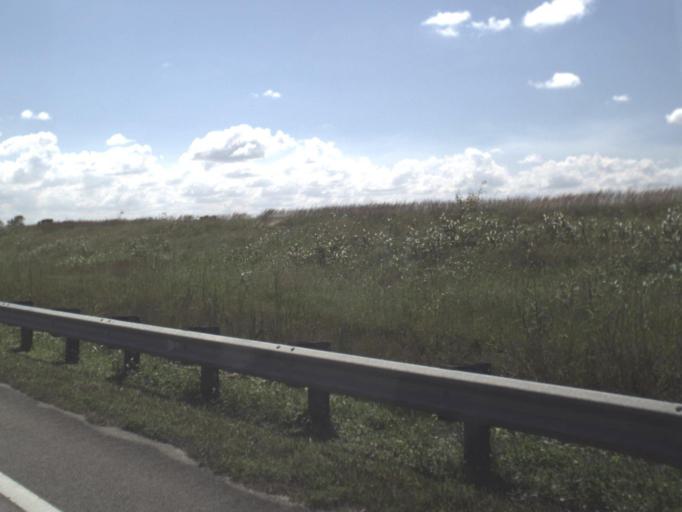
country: US
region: Florida
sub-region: Glades County
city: Moore Haven
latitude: 26.8737
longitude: -81.1227
